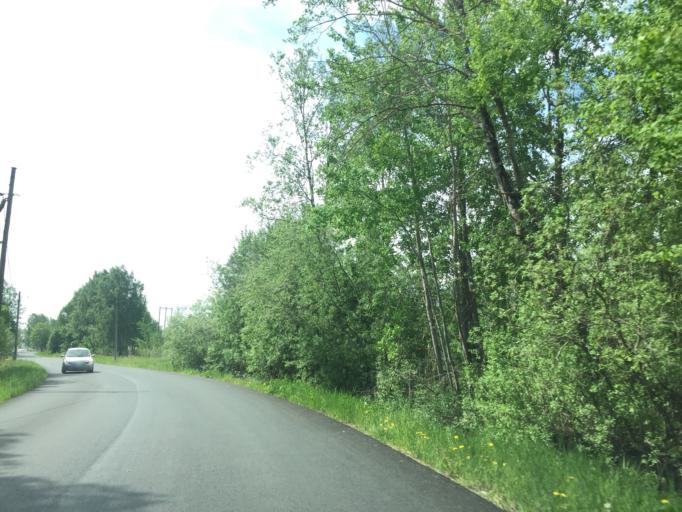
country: SE
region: OErebro
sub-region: Orebro Kommun
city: Orebro
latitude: 59.2783
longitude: 15.2509
